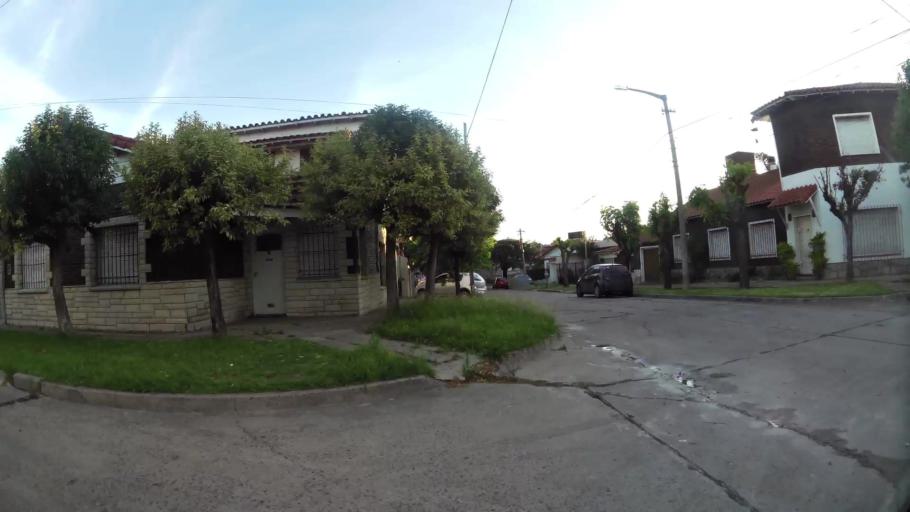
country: AR
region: Buenos Aires
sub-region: Partido de Moron
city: Moron
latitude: -34.6488
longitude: -58.6323
